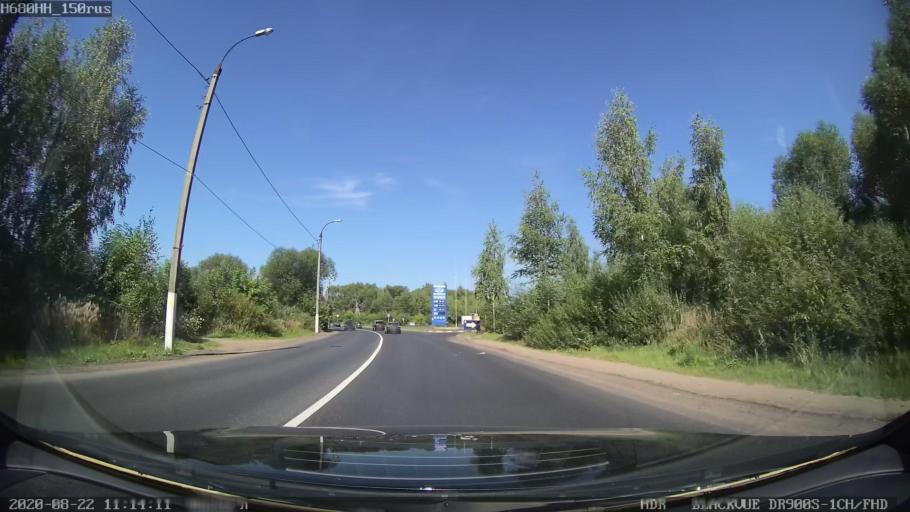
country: RU
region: Tverskaya
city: Tver
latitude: 56.8740
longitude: 35.9415
